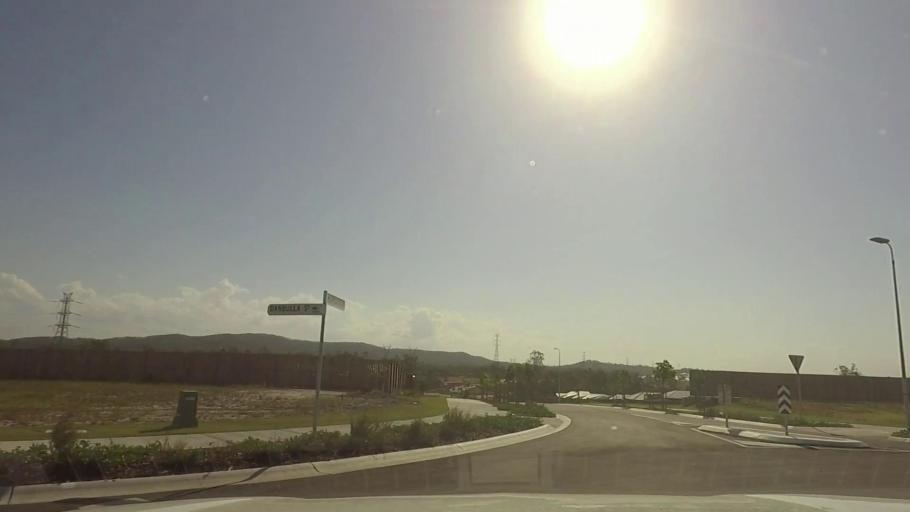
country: AU
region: Queensland
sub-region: Logan
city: Chambers Flat
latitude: -27.8171
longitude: 153.1305
